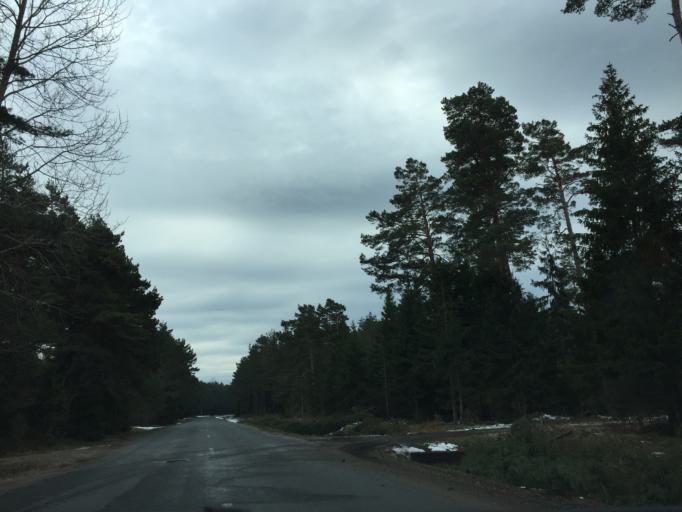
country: EE
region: Saare
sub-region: Kuressaare linn
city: Kuressaare
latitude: 58.4287
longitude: 22.0719
